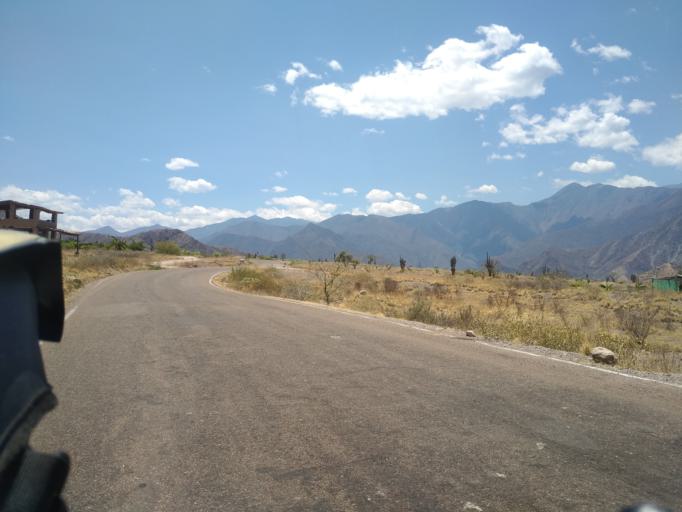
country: PE
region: Amazonas
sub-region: Provincia de Chachapoyas
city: Balsas
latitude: -6.8485
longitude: -78.0355
